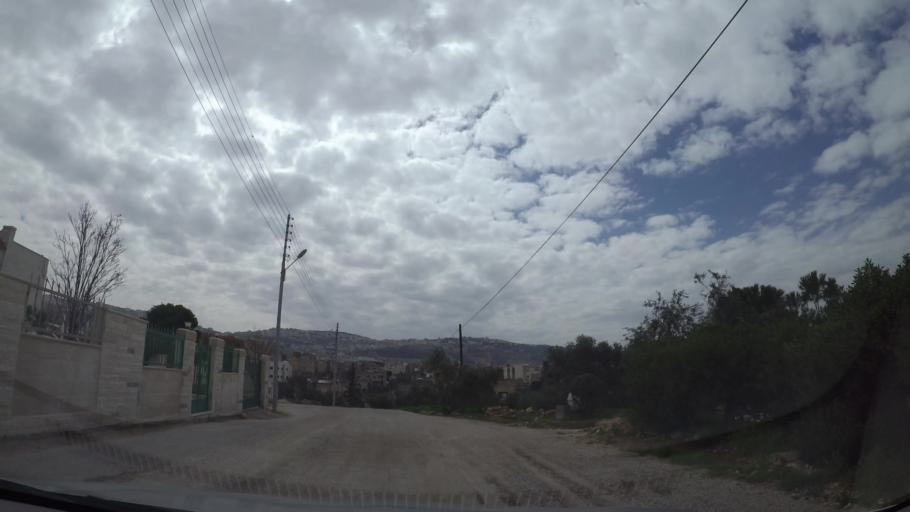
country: JO
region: Amman
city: Al Jubayhah
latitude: 32.0622
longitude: 35.8330
